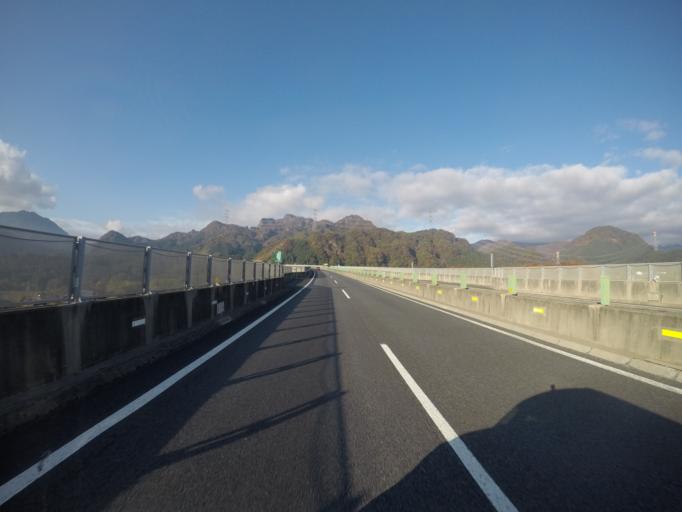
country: JP
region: Gunma
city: Annaka
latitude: 36.3447
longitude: 138.7250
